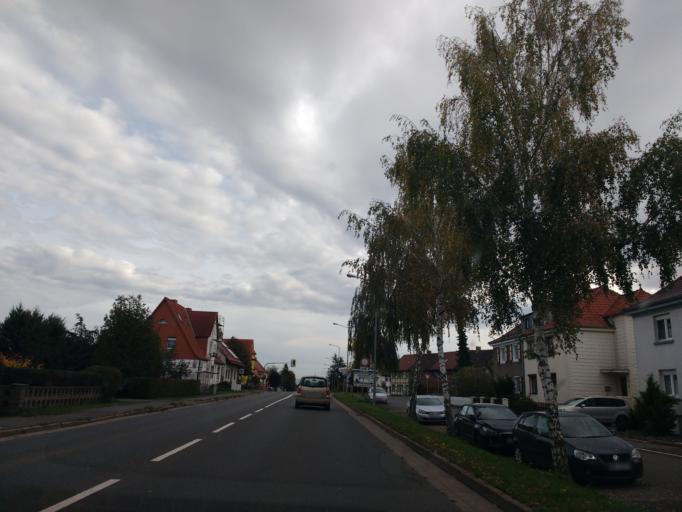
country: DE
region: Thuringia
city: Uthleben
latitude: 51.4863
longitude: 10.8397
